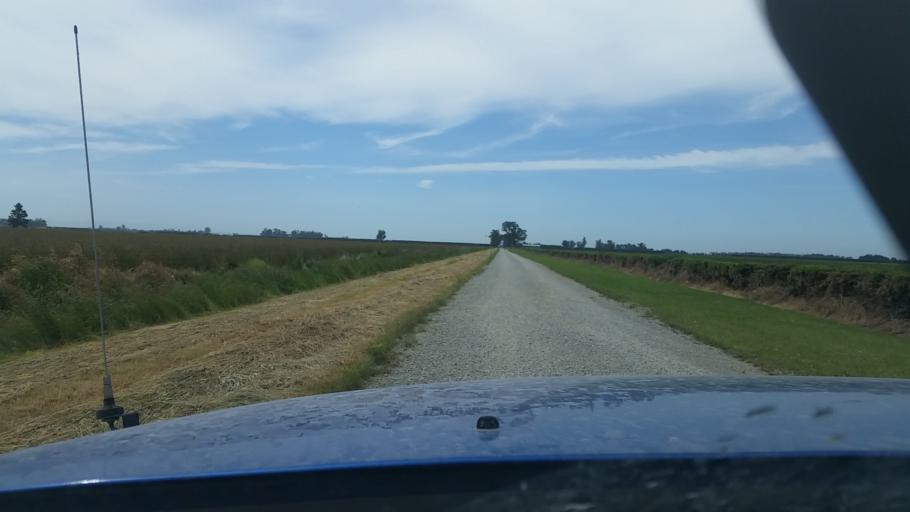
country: NZ
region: Canterbury
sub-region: Ashburton District
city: Tinwald
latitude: -44.0566
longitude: 171.7689
